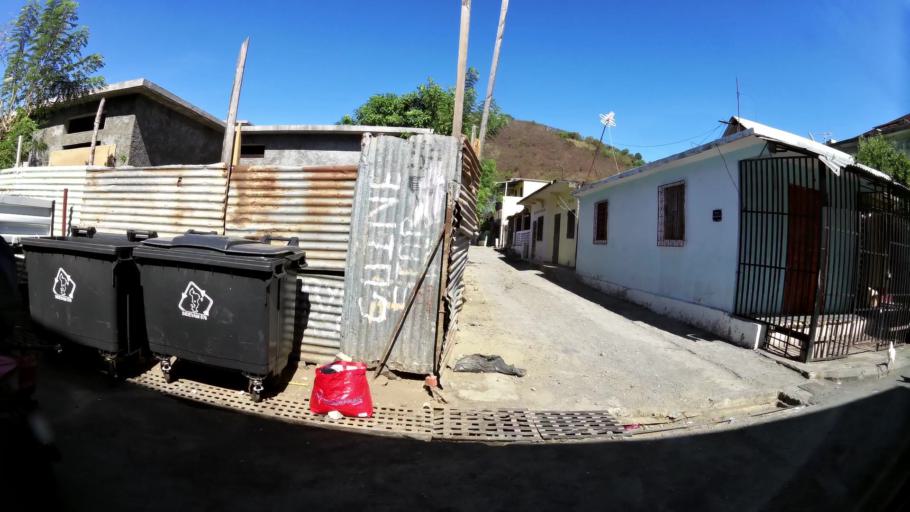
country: YT
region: Pamandzi
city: Pamandzi
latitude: -12.7872
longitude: 45.2734
